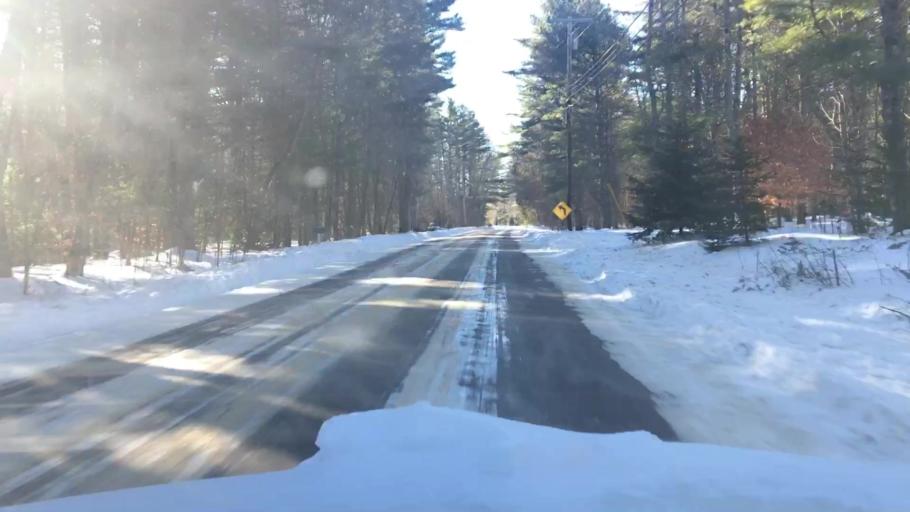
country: US
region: Maine
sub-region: Cumberland County
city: Brunswick
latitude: 43.9541
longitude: -69.9295
